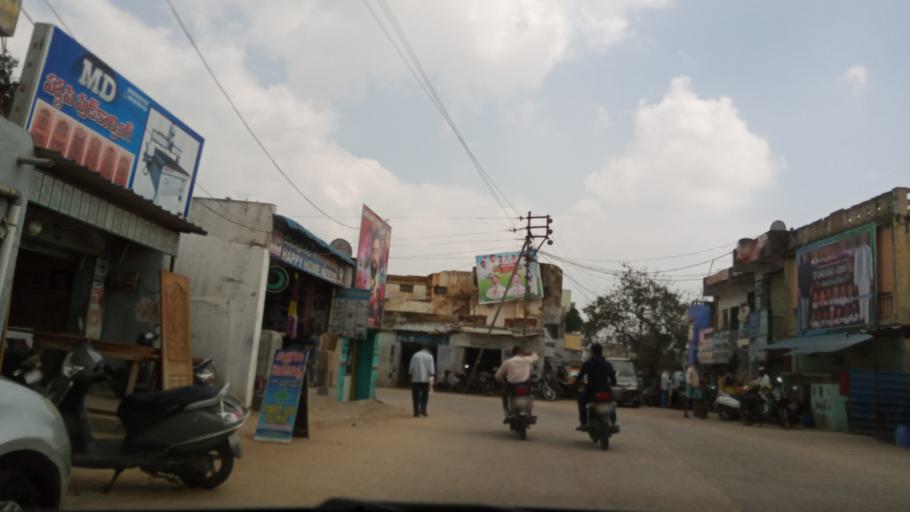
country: IN
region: Andhra Pradesh
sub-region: Chittoor
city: Madanapalle
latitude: 13.6378
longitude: 78.6307
